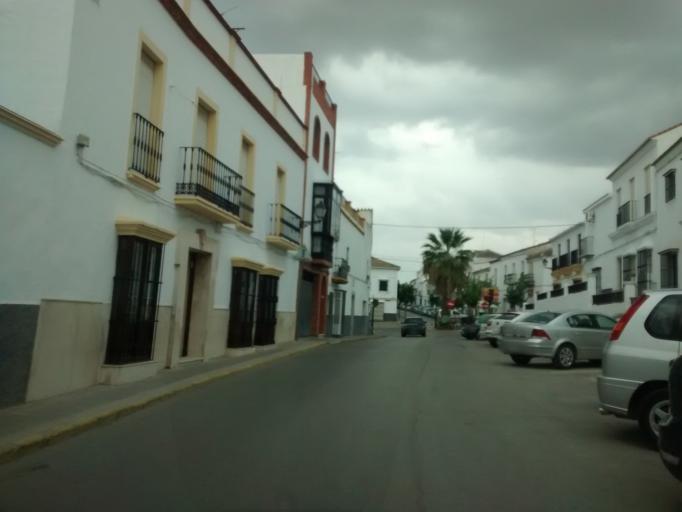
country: ES
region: Andalusia
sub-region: Provincia de Cadiz
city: Bornos
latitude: 36.8158
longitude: -5.7455
